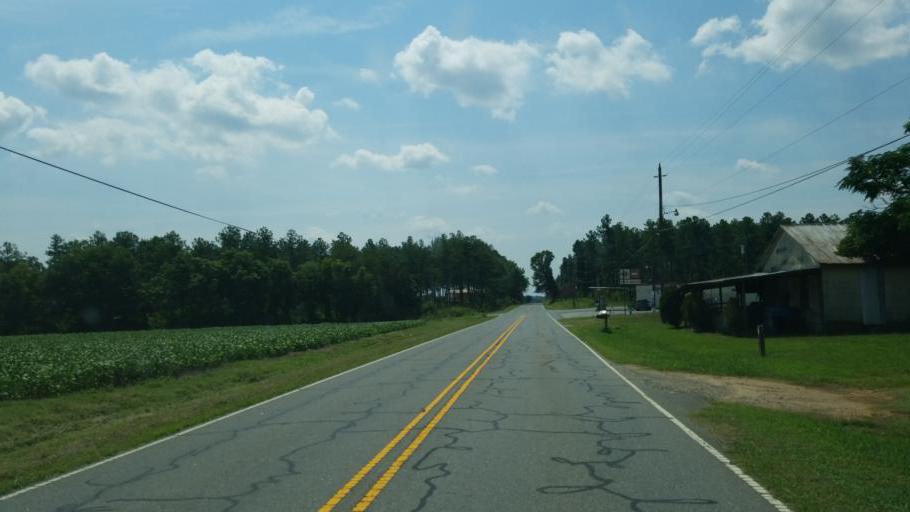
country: US
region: North Carolina
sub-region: Gaston County
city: Cherryville
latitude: 35.4423
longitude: -81.4249
